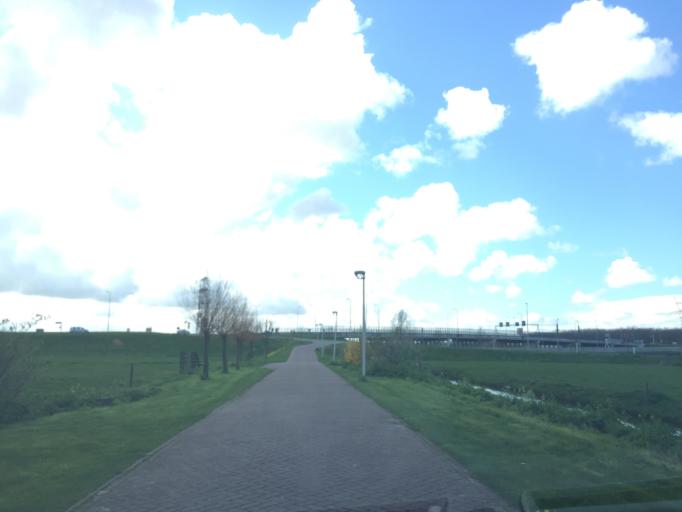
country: NL
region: South Holland
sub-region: Gemeente Leiderdorp
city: Leiderdorp
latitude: 52.1633
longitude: 4.5627
